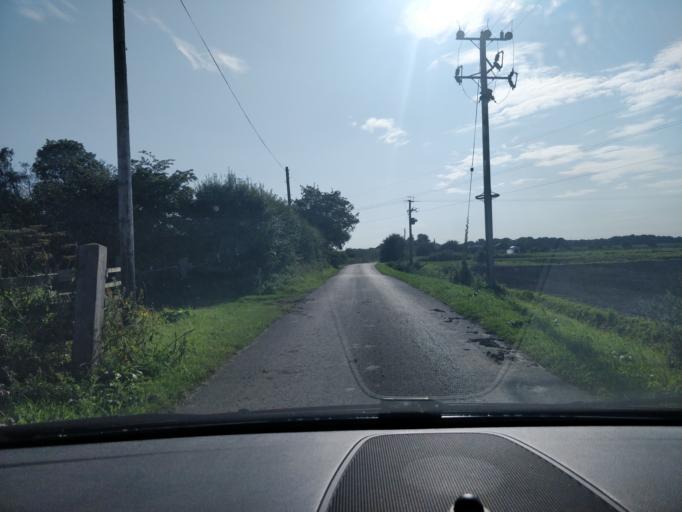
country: GB
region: England
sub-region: Lancashire
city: Banks
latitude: 53.6547
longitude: -2.9278
